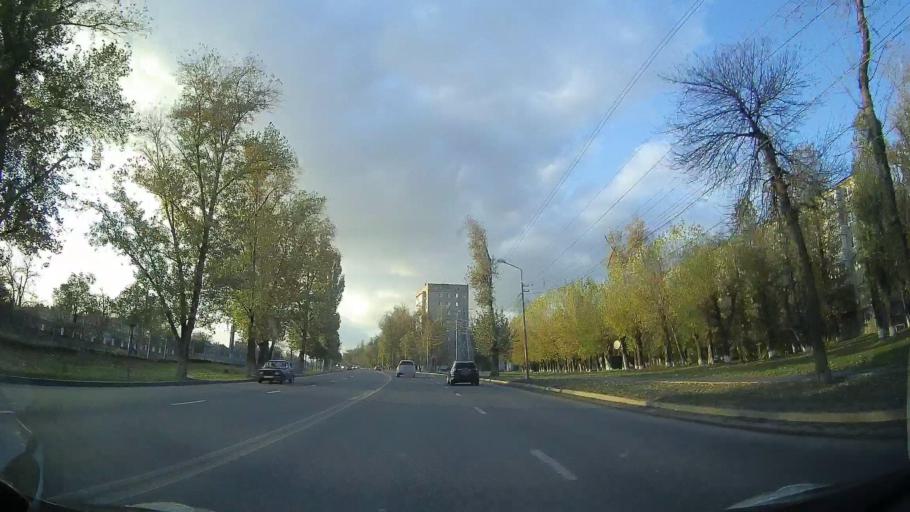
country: RU
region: Rostov
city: Imeni Chkalova
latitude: 47.2594
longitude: 39.7902
